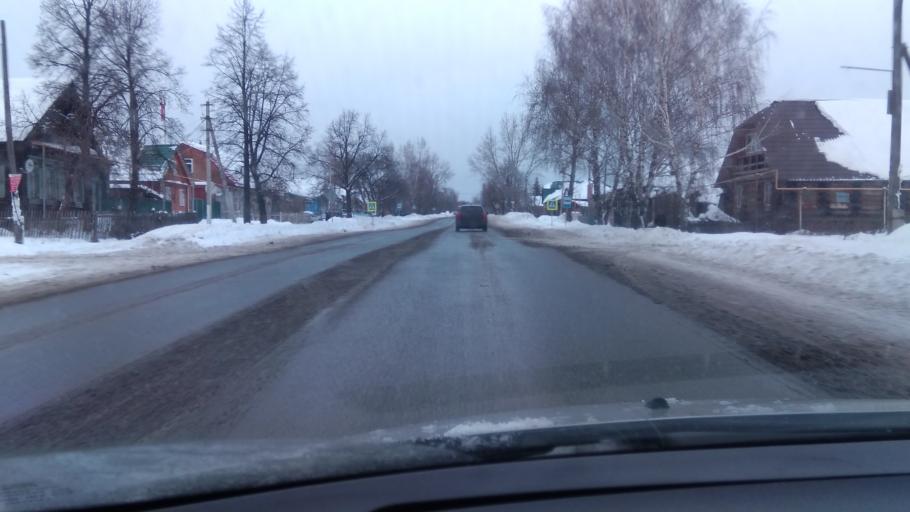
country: RU
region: Sverdlovsk
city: Nikolo-Pavlovskoye
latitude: 57.7872
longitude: 60.0553
